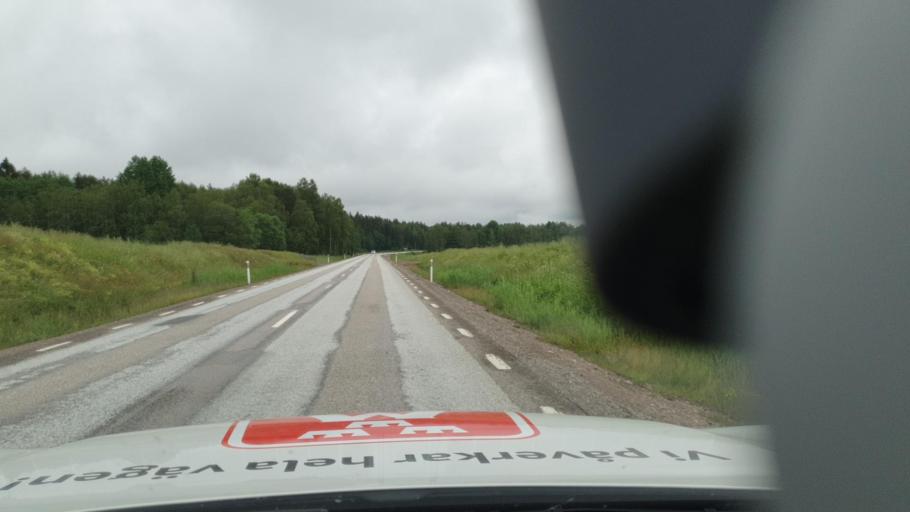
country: SE
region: Vaermland
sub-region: Kristinehamns Kommun
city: Bjorneborg
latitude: 59.2524
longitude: 14.1887
